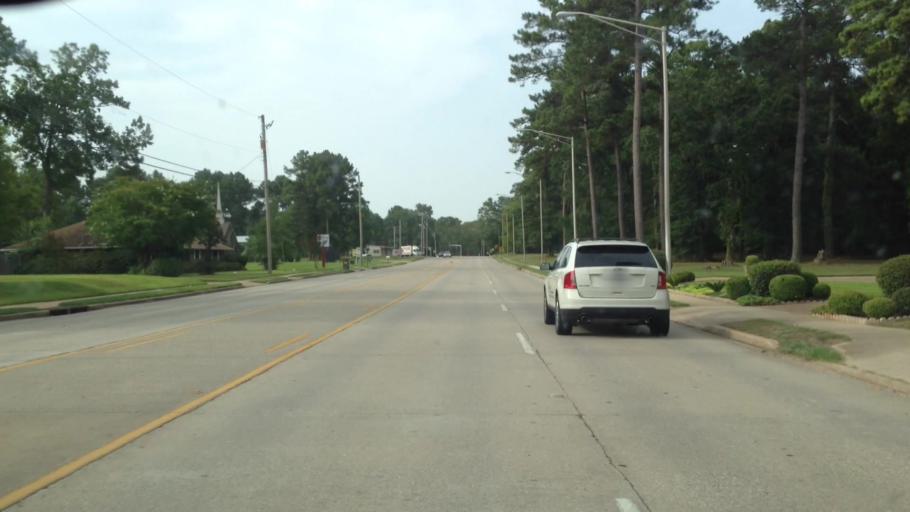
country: US
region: Louisiana
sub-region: De Soto Parish
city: Stonewall
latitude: 32.3980
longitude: -93.8147
